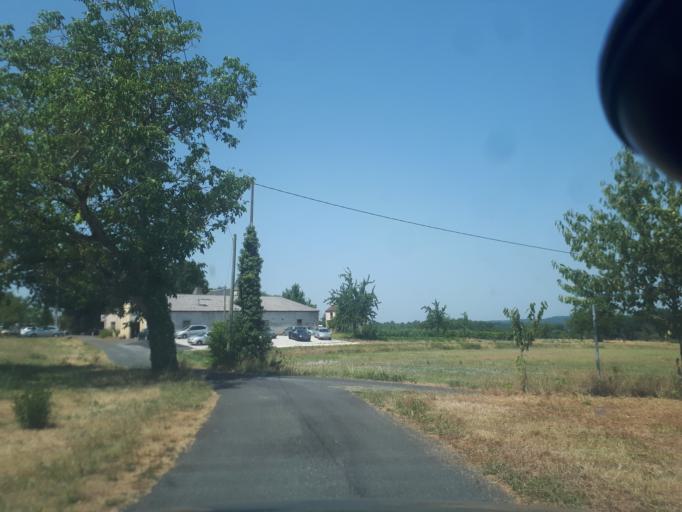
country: FR
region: Midi-Pyrenees
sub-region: Departement du Lot
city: Salviac
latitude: 44.7357
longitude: 1.3002
